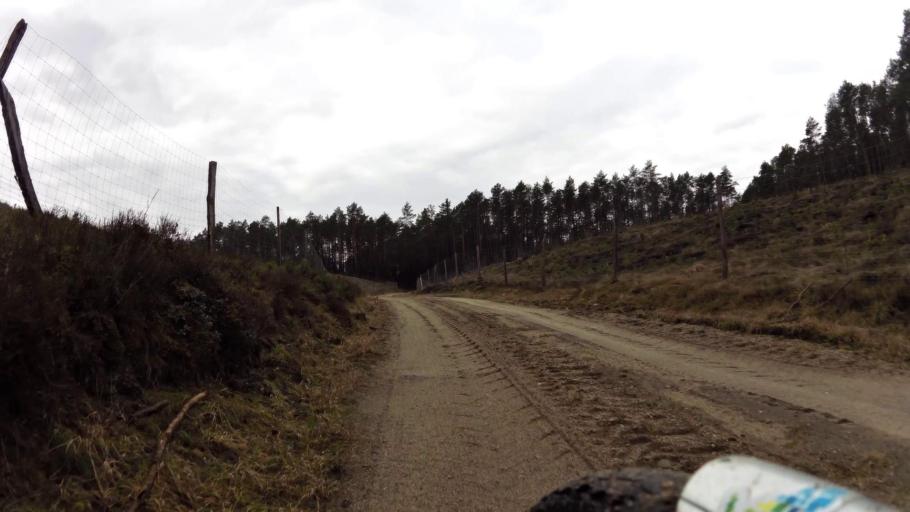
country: PL
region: Pomeranian Voivodeship
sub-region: Powiat bytowski
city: Borzytuchom
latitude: 54.2616
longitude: 17.3855
